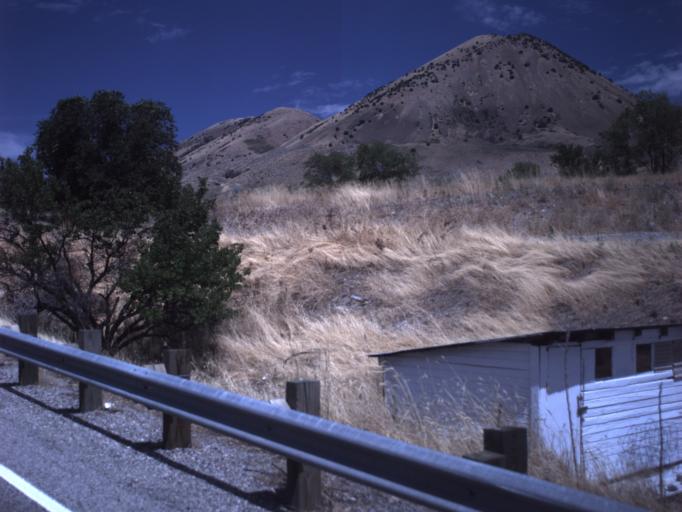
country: US
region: Utah
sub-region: Box Elder County
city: Elwood
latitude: 41.7165
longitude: -112.0928
